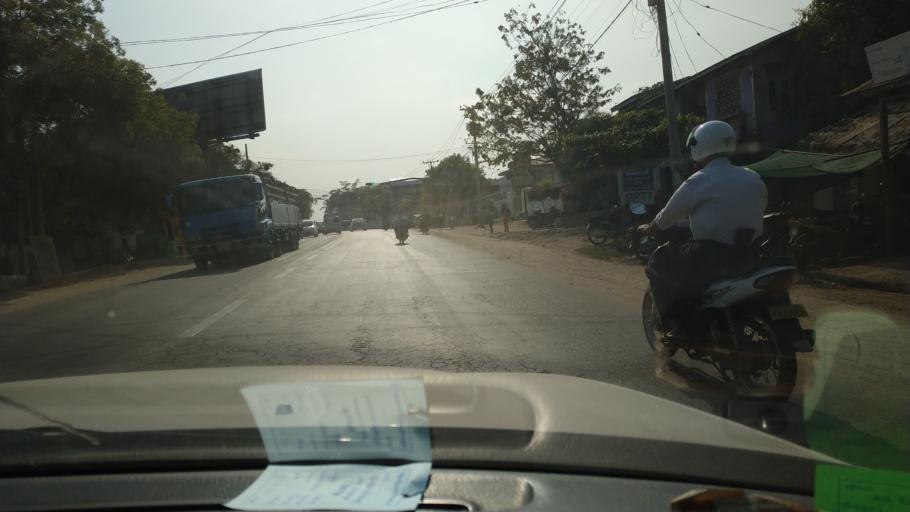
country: MM
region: Mandalay
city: Meiktila
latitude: 20.8744
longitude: 95.8412
